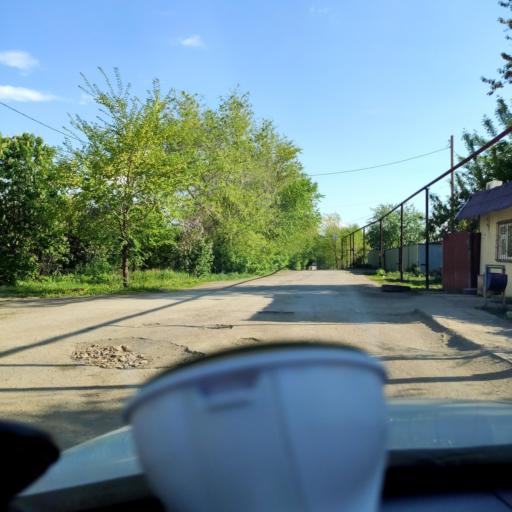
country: RU
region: Samara
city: Petra-Dubrava
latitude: 53.2579
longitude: 50.3441
